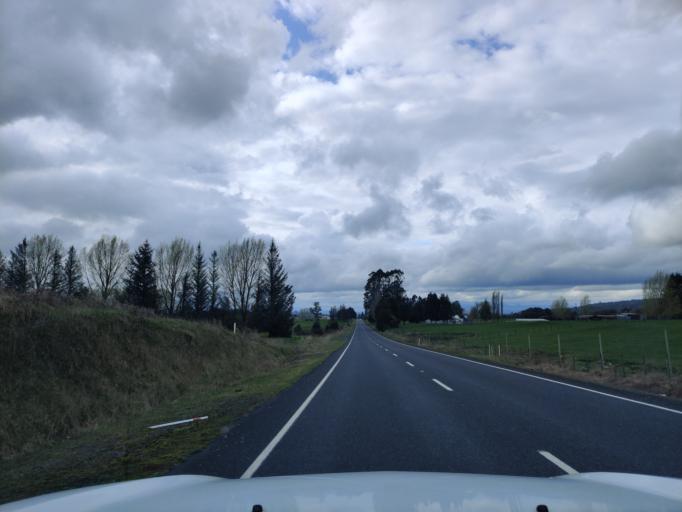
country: NZ
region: Waikato
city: Turangi
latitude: -39.0494
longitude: 175.3836
